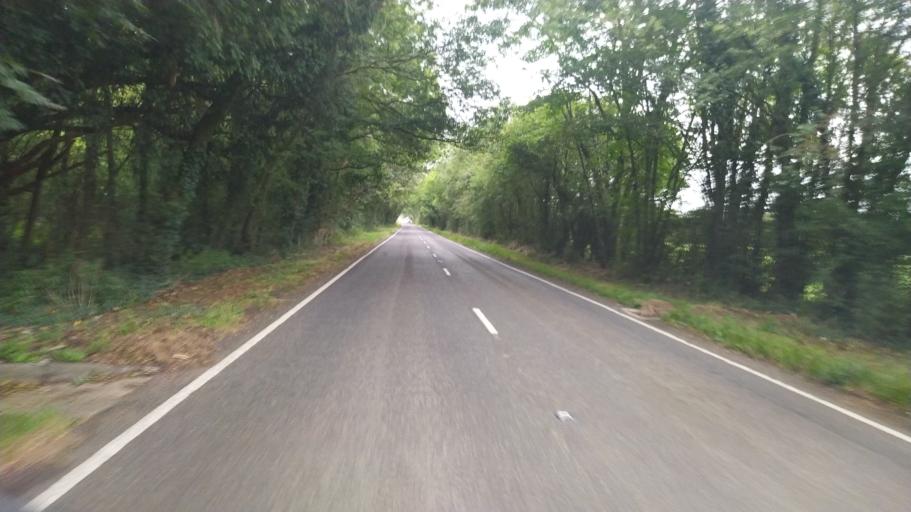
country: GB
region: England
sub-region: Dorset
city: Sherborne
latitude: 50.8833
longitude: -2.4867
